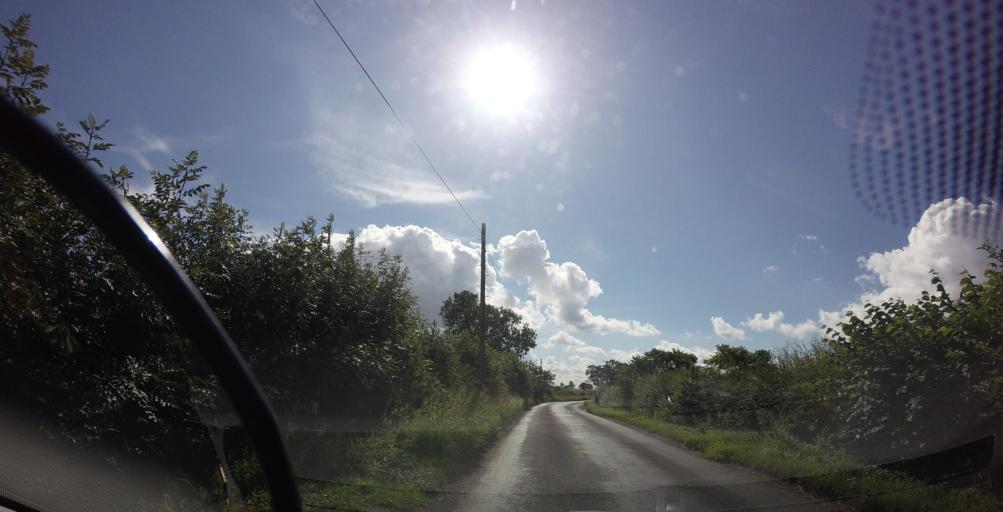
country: GB
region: England
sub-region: North Yorkshire
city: Ripon
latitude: 54.0877
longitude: -1.4969
